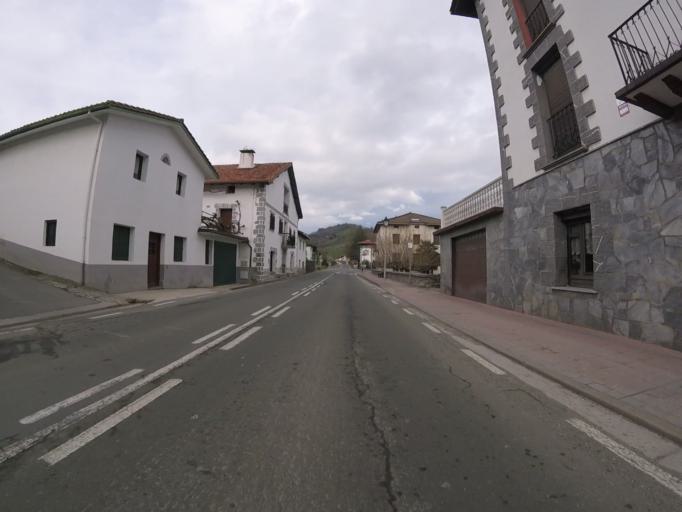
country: ES
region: Basque Country
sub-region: Provincia de Guipuzcoa
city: Albiztur
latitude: 43.1374
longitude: -2.1605
